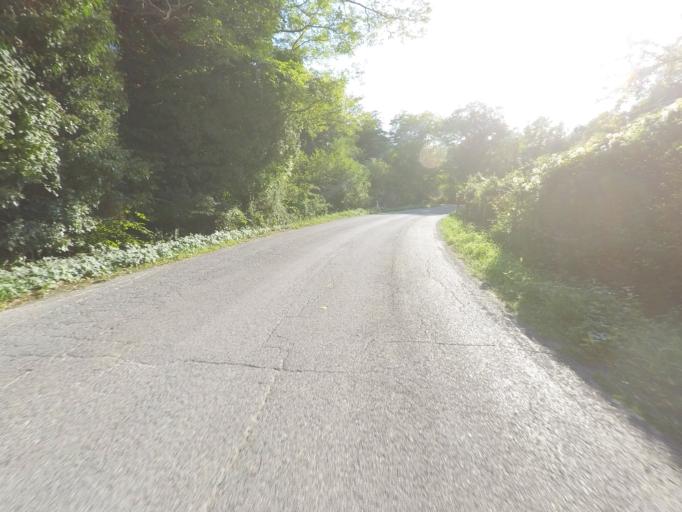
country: IT
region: Tuscany
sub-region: Provincia di Siena
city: Radda in Chianti
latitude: 43.4690
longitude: 11.3741
